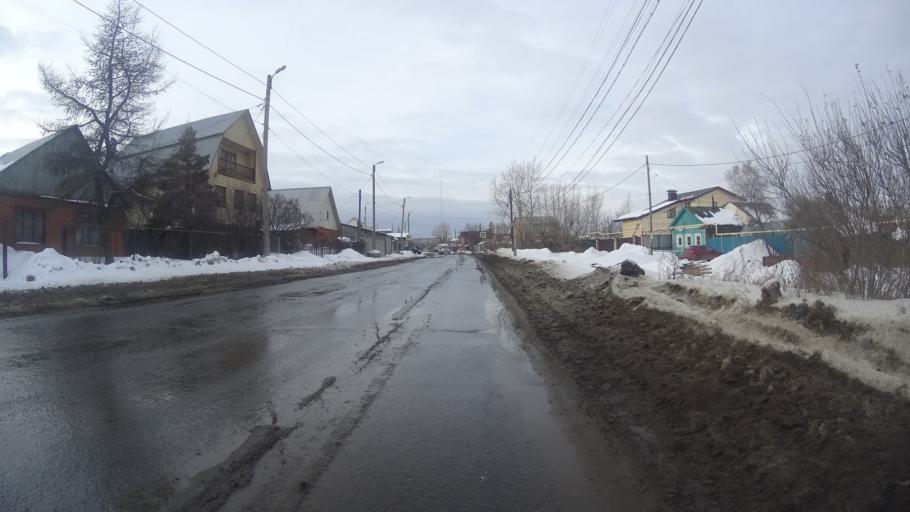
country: RU
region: Chelyabinsk
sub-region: Gorod Chelyabinsk
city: Chelyabinsk
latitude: 55.1298
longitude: 61.3985
